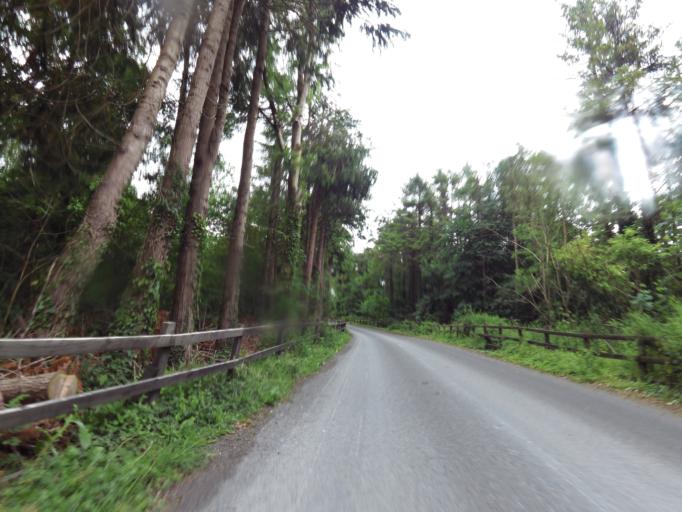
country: IE
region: Connaught
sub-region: County Galway
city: Athenry
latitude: 53.2835
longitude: -8.6830
